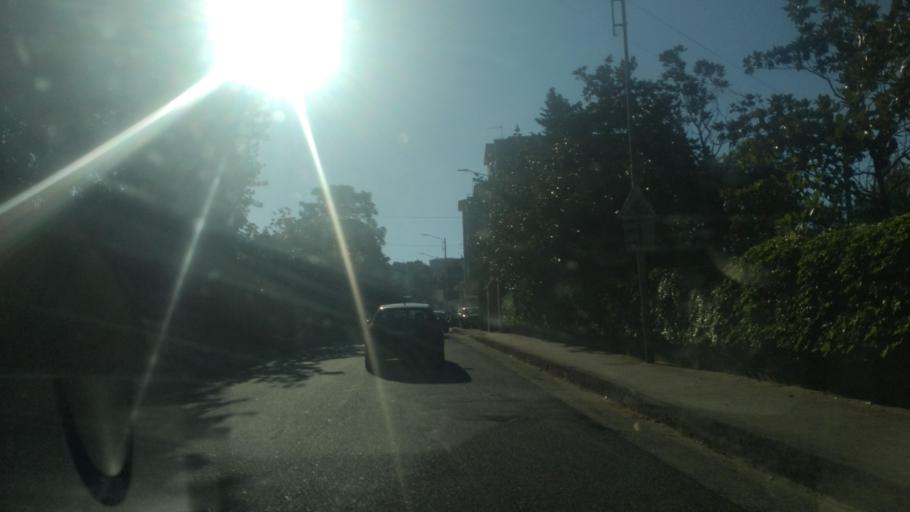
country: IT
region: Calabria
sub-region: Provincia di Catanzaro
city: Squillace
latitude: 38.7809
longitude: 16.5128
